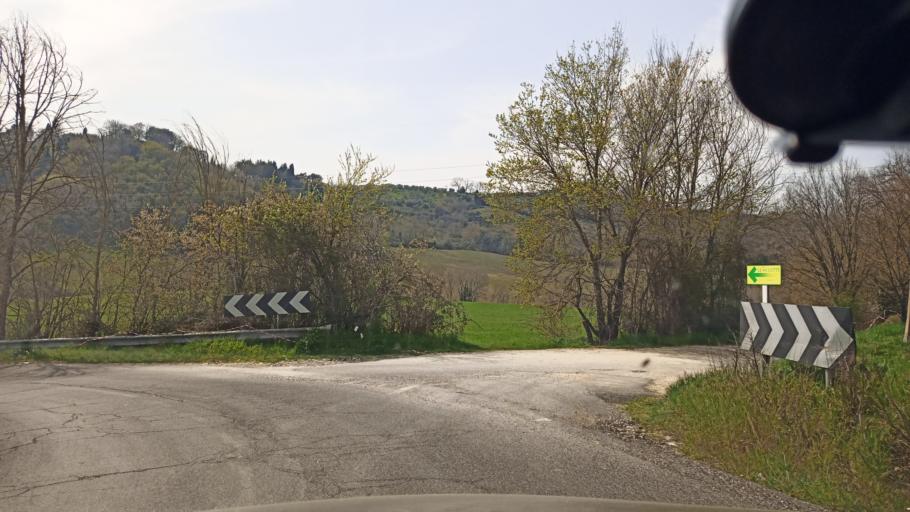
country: IT
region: Latium
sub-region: Provincia di Rieti
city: Cantalupo in Sabina
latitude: 42.3271
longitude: 12.6422
